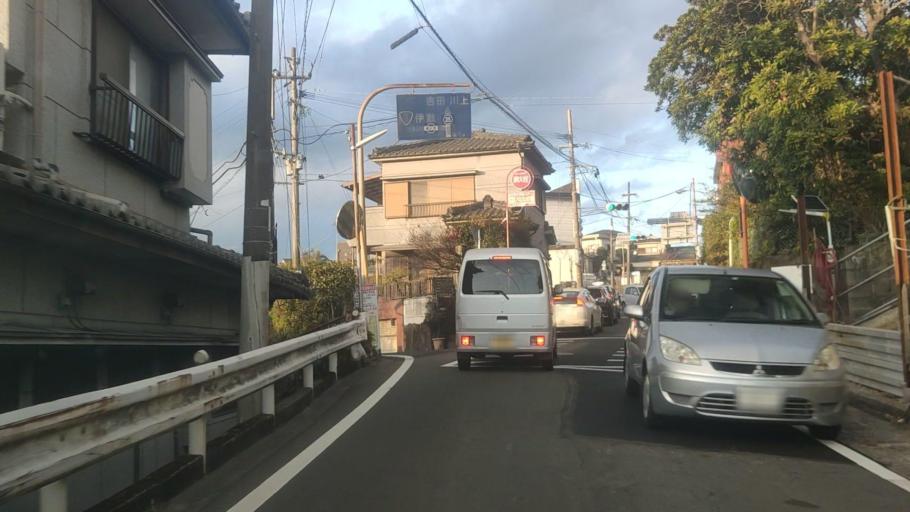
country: JP
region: Kagoshima
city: Kagoshima-shi
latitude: 31.6240
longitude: 130.5527
